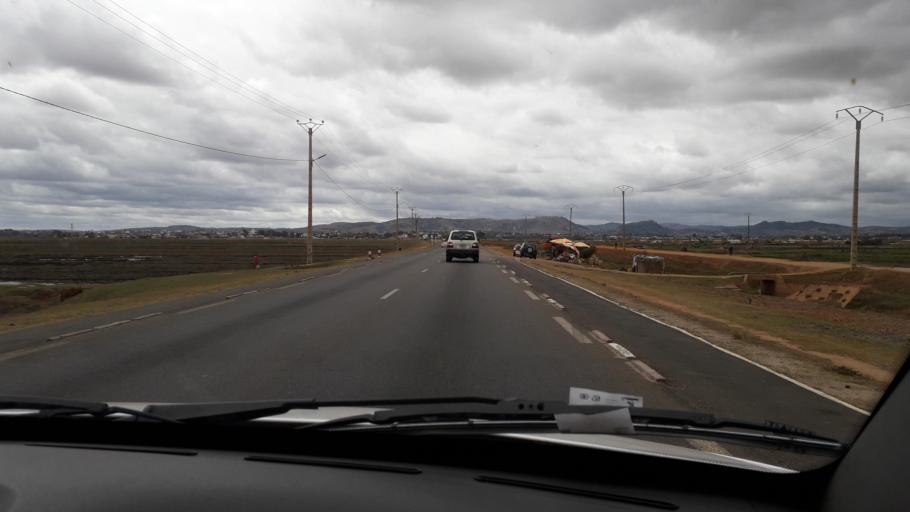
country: MG
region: Analamanga
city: Antananarivo
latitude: -18.8246
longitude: 47.5147
